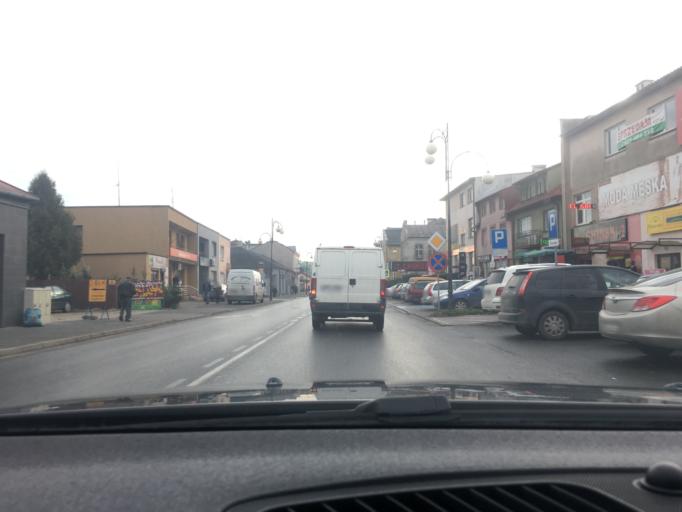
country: PL
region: Swietokrzyskie
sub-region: Powiat jedrzejowski
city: Jedrzejow
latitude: 50.6412
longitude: 20.3016
